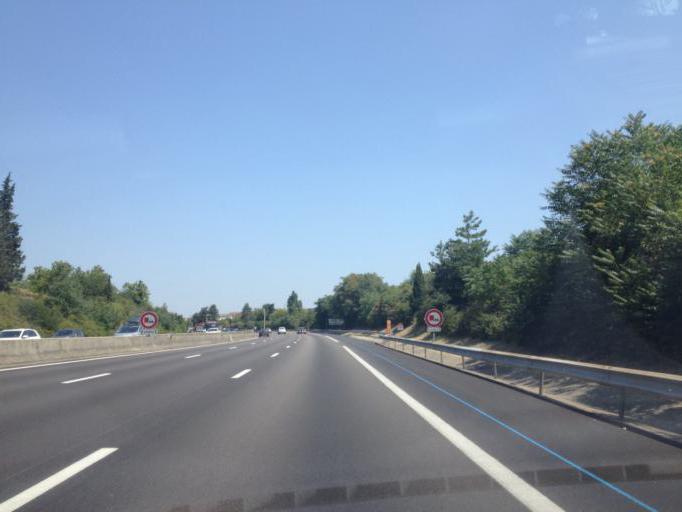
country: FR
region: Rhone-Alpes
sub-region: Departement de la Drome
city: Valence
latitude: 44.9442
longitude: 4.8905
